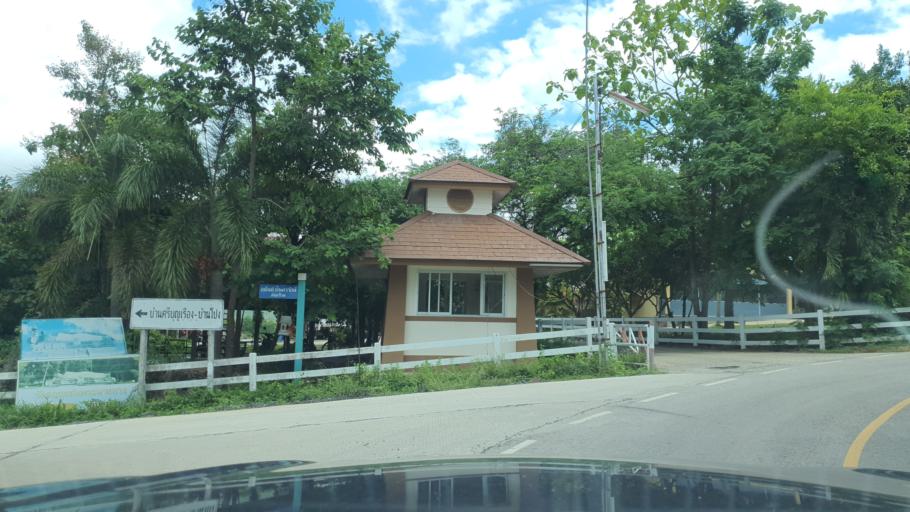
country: TH
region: Chiang Mai
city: San Sai
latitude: 18.9179
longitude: 99.0509
